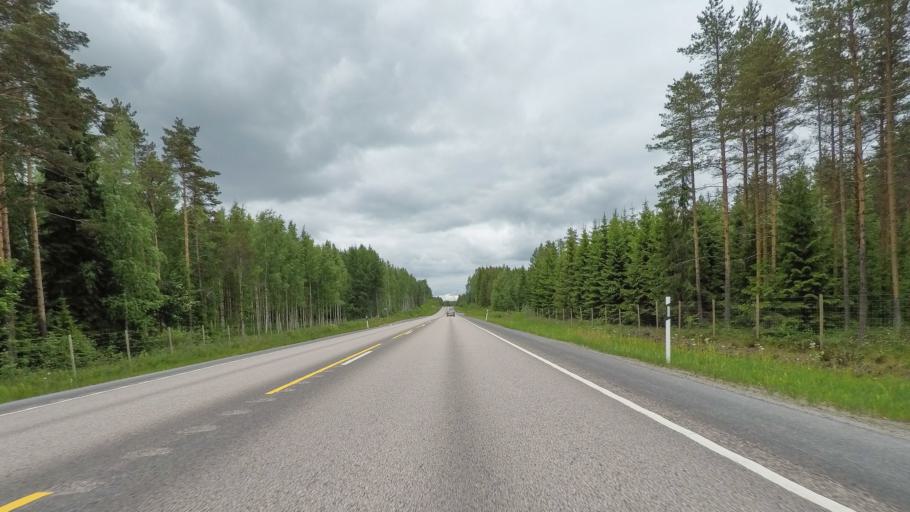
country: FI
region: Central Finland
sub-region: Joutsa
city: Leivonmaeki
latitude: 61.8375
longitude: 26.0973
